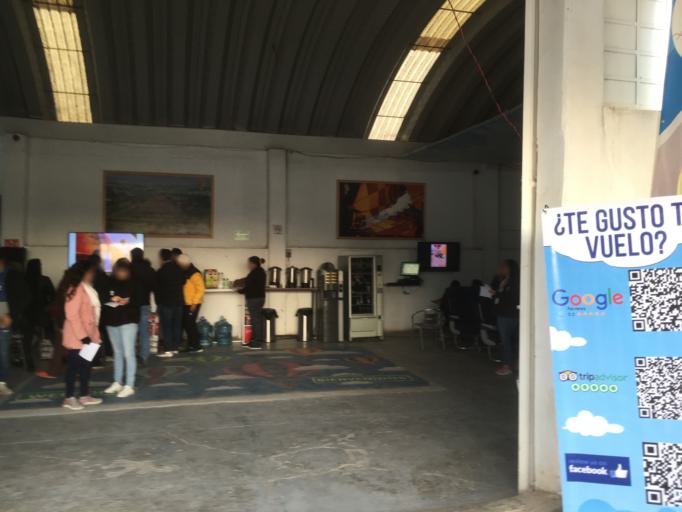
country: MX
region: Morelos
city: San Martin de las Piramides
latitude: 19.6997
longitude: -98.8213
